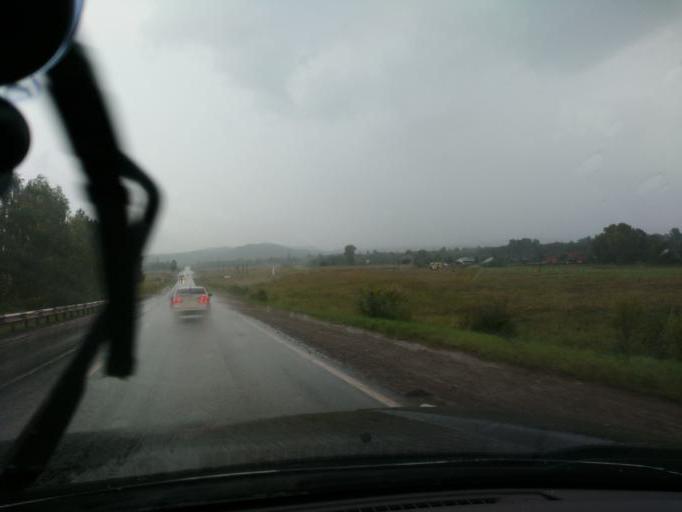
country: RU
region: Perm
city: Osa
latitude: 57.1803
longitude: 55.5469
